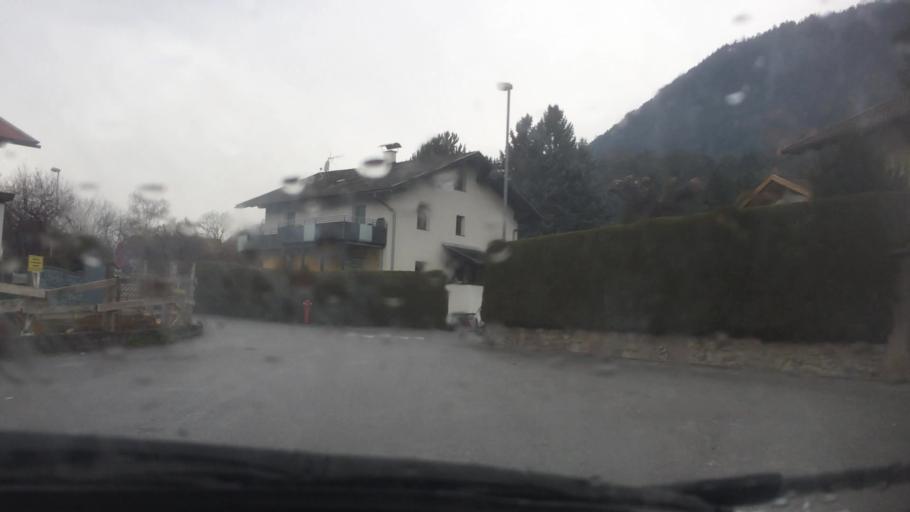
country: AT
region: Tyrol
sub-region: Politischer Bezirk Innsbruck Land
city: Pfaffenhofen
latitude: 47.3173
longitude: 11.0963
